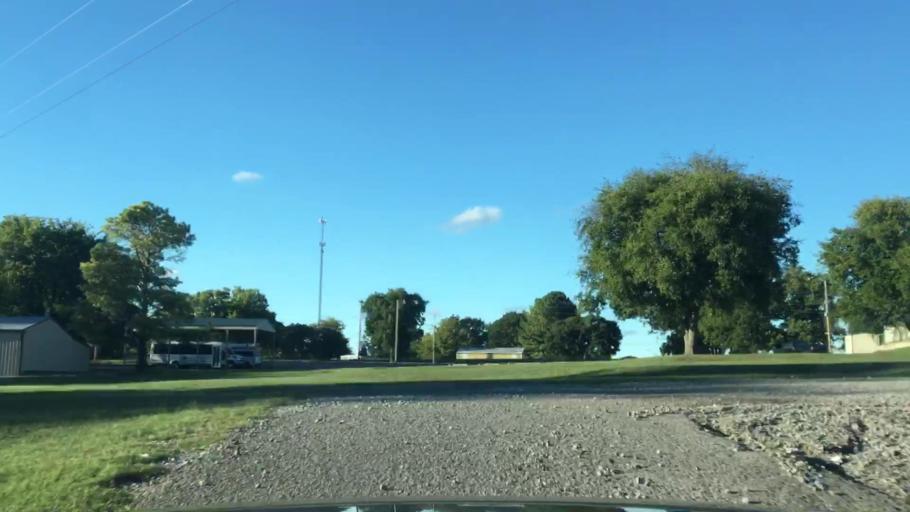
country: US
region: Oklahoma
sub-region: Cherokee County
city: Park Hill
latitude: 35.8023
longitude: -95.0905
